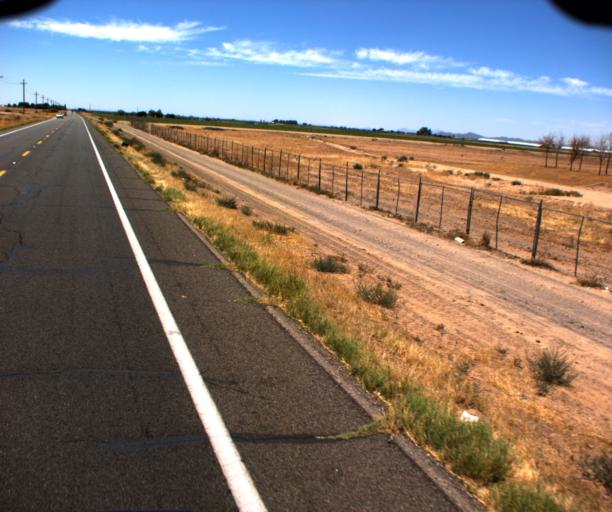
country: US
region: Arizona
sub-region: Pinal County
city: Casa Grande
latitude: 32.8798
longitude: -111.6341
